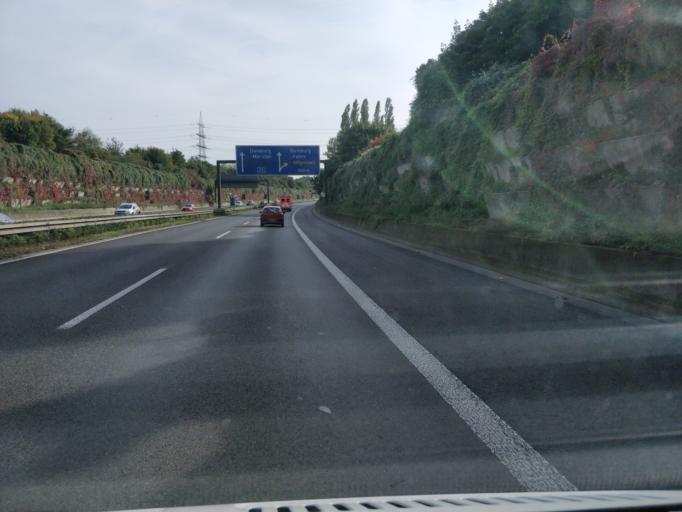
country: DE
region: North Rhine-Westphalia
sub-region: Regierungsbezirk Dusseldorf
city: Dinslaken
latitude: 51.5203
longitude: 6.7600
